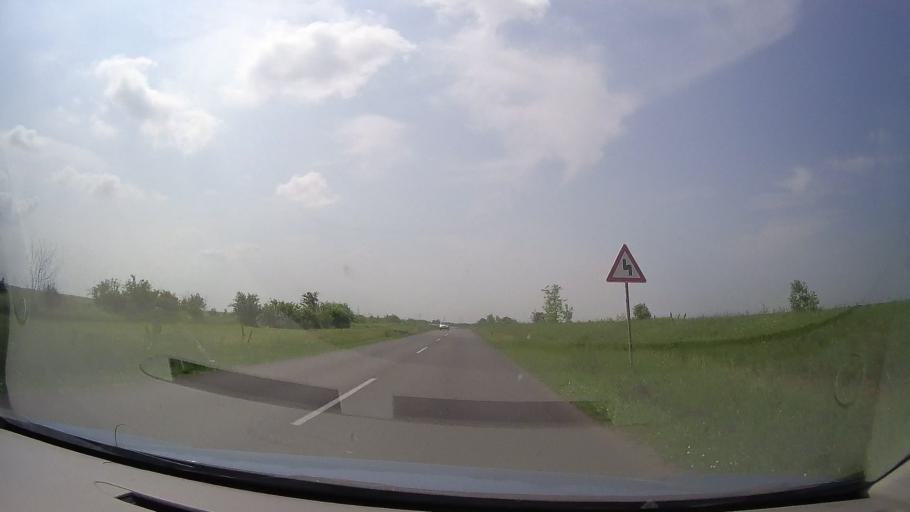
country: RS
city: Crepaja
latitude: 44.9784
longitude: 20.6466
